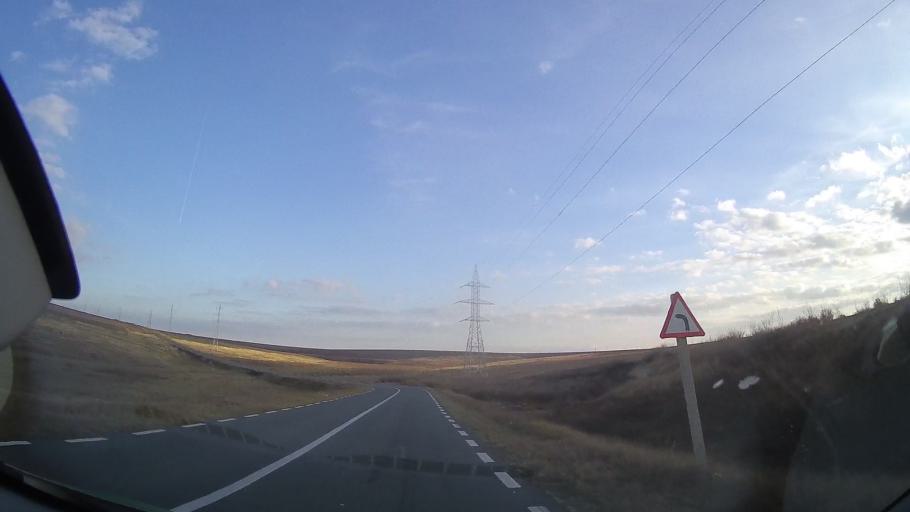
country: RO
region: Constanta
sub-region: Comuna Chirnogeni
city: Plopeni
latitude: 43.9548
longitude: 28.1503
